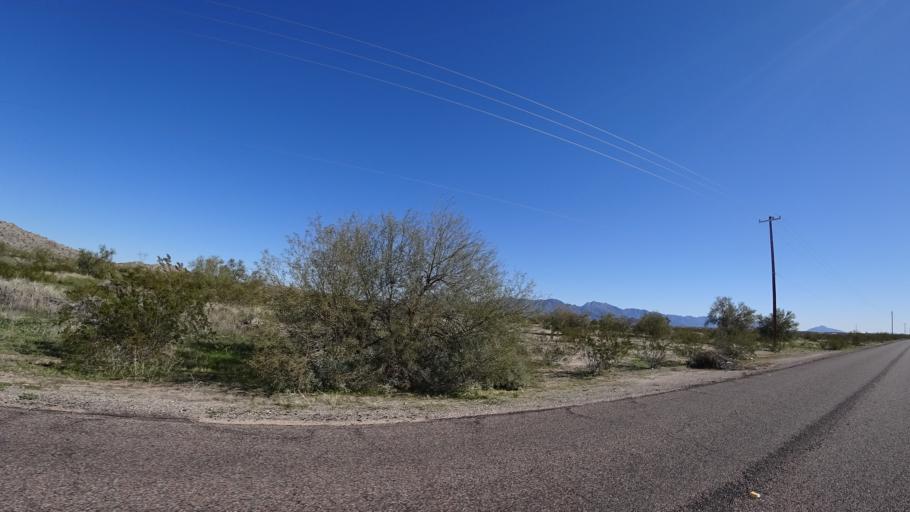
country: US
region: Arizona
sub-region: Maricopa County
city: Buckeye
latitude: 33.3048
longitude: -112.4609
